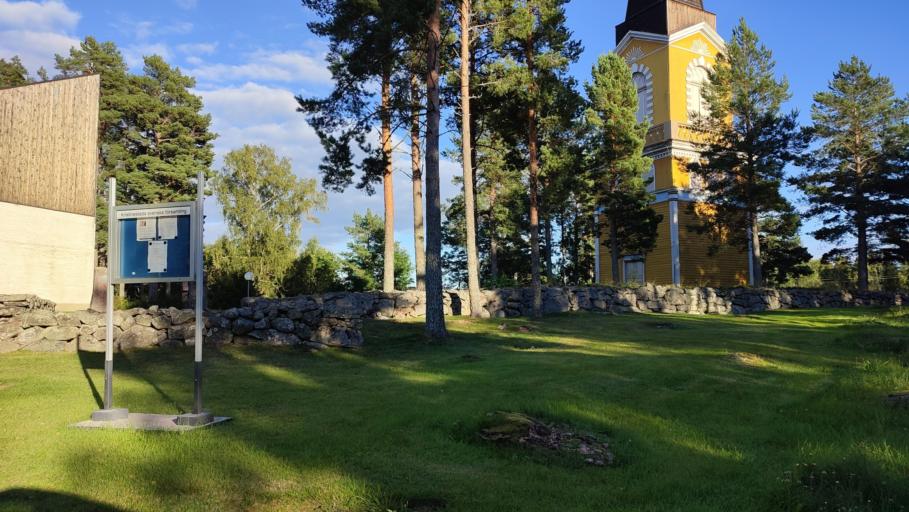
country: FI
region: Satakunta
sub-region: Pori
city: Merikarvia
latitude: 62.0304
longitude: 21.3301
